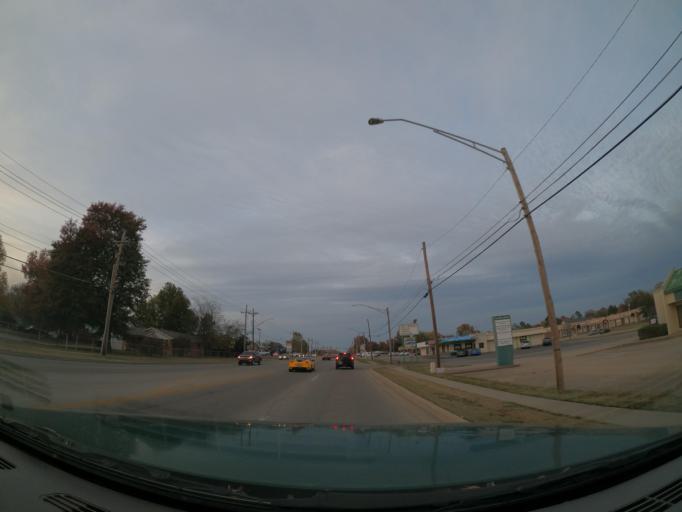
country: US
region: Oklahoma
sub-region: Tulsa County
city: Broken Arrow
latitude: 36.0298
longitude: -95.7974
